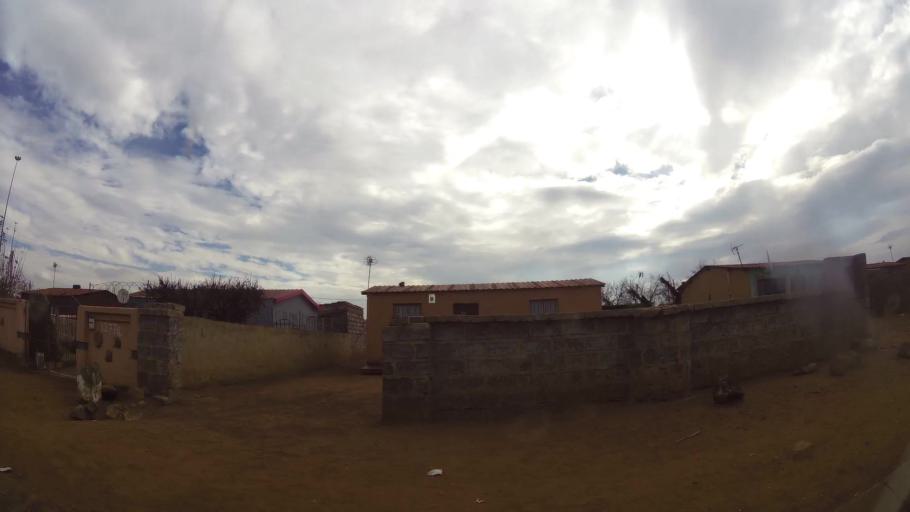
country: ZA
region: Gauteng
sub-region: Ekurhuleni Metropolitan Municipality
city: Germiston
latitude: -26.4094
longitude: 28.1576
